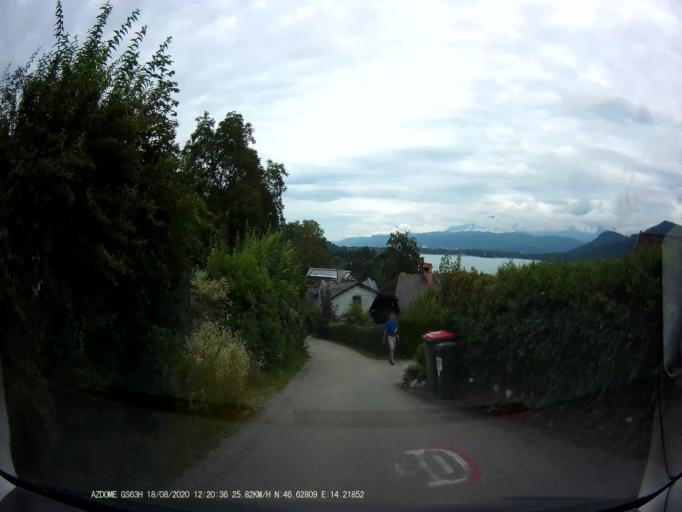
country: AT
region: Carinthia
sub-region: Politischer Bezirk Klagenfurt Land
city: Keutschach am See
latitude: 46.6281
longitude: 14.2187
